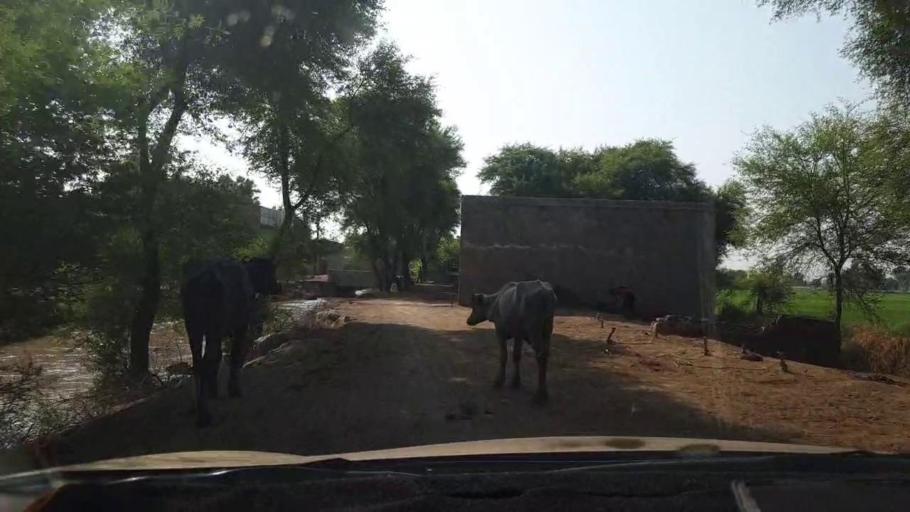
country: PK
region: Sindh
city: Larkana
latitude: 27.6229
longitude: 68.2616
